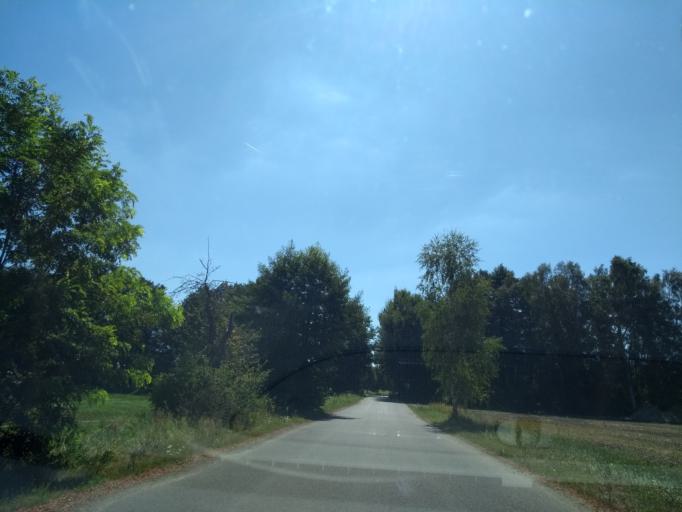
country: DE
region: Brandenburg
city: Lubbenau
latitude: 51.8325
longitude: 13.9515
